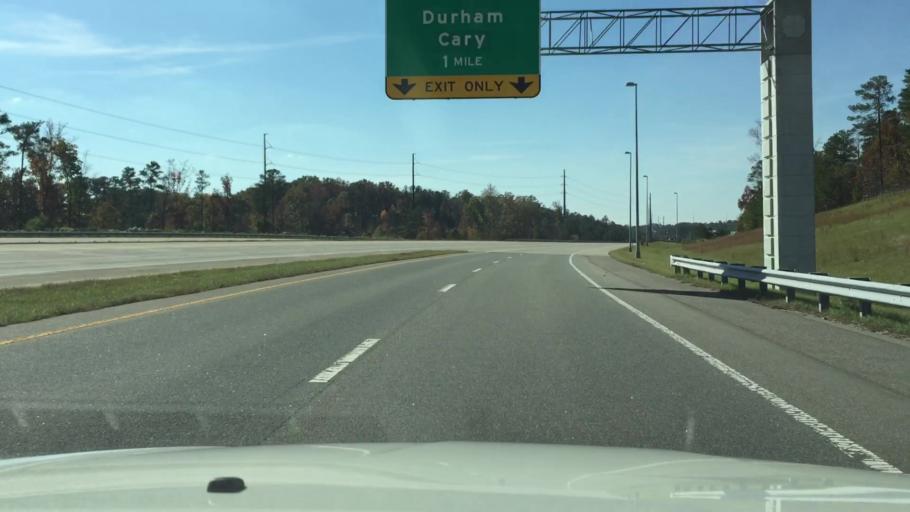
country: US
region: North Carolina
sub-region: Wake County
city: Morrisville
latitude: 35.8483
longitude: -78.8675
